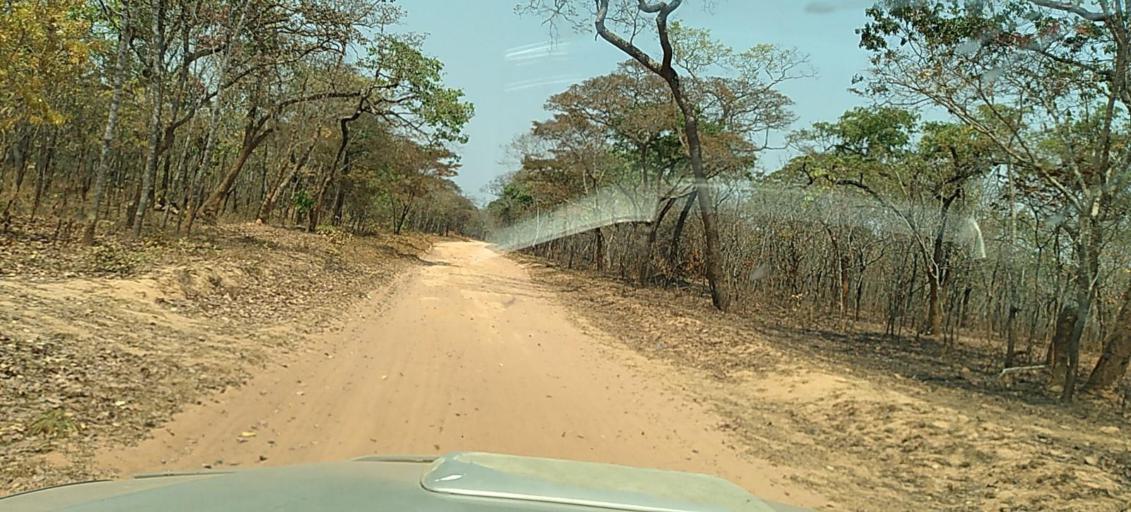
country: ZM
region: North-Western
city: Kasempa
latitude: -13.6577
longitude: 26.2636
